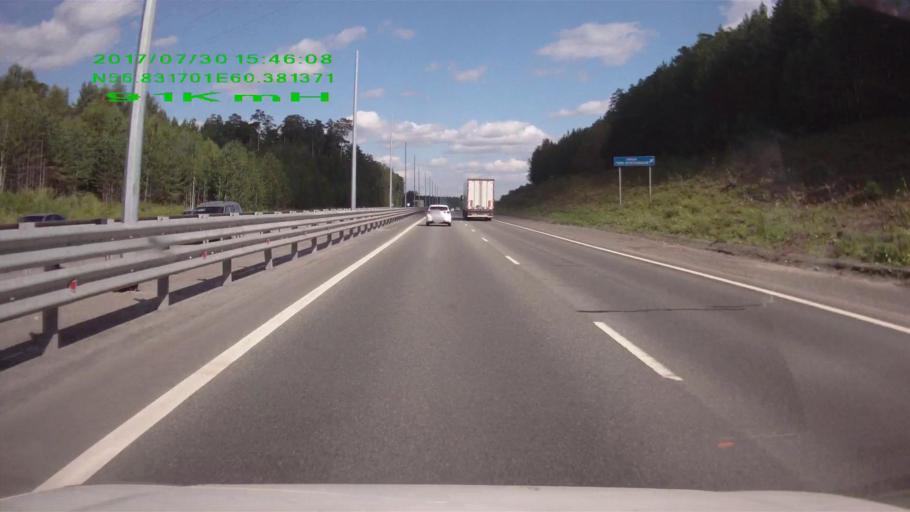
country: RU
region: Sverdlovsk
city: Severka
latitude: 56.8317
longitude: 60.3820
